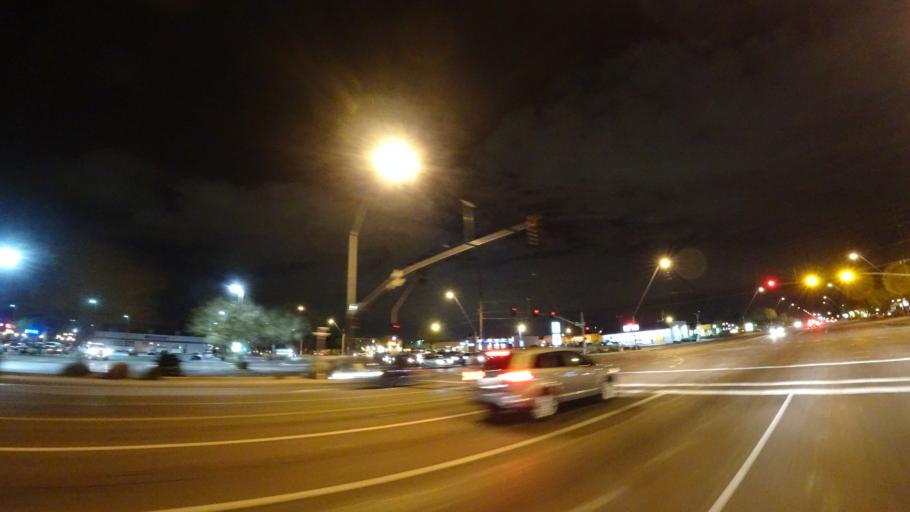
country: US
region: Arizona
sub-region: Maricopa County
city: San Carlos
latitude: 33.3639
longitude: -111.8590
